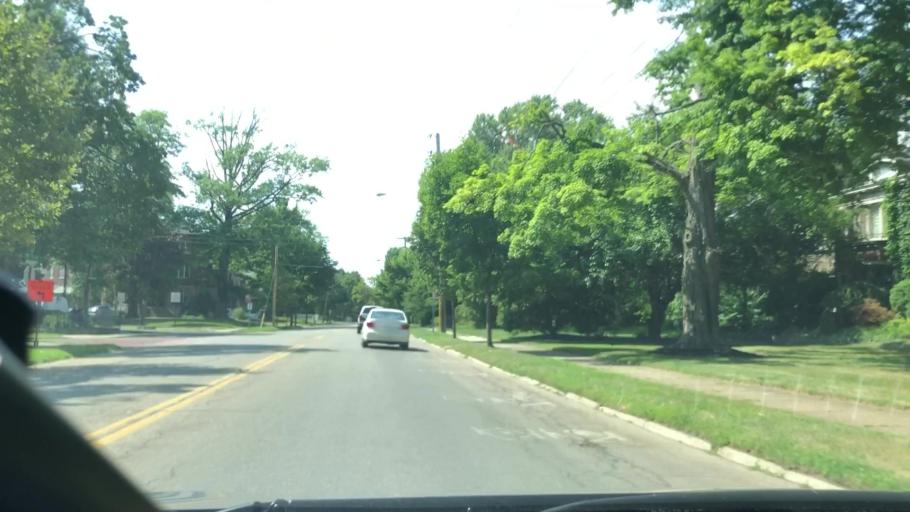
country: US
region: Ohio
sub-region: Summit County
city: Akron
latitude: 41.0994
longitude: -81.5491
